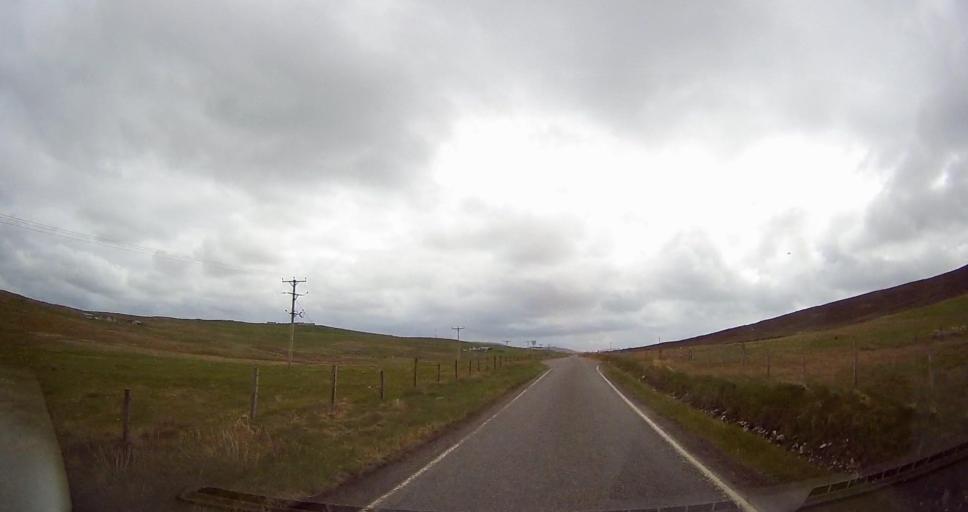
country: GB
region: Scotland
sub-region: Shetland Islands
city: Sandwick
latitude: 60.2487
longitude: -1.5088
